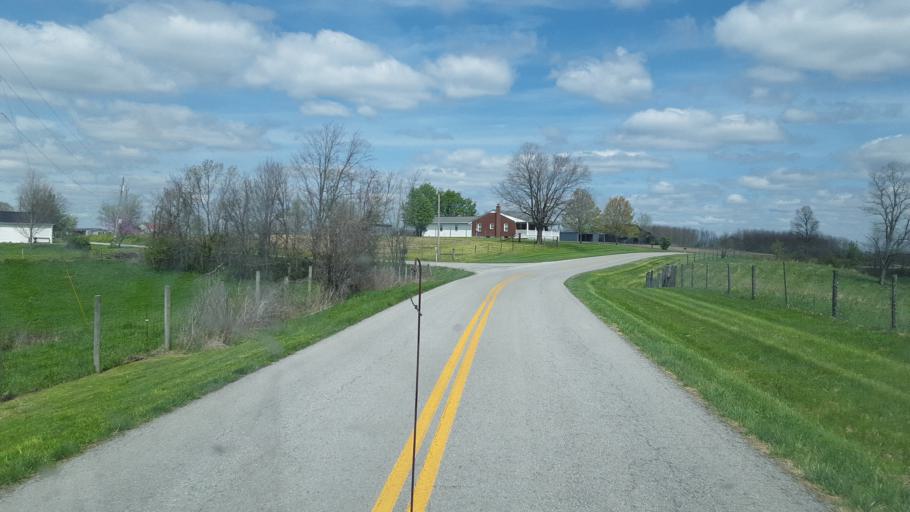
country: US
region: Kentucky
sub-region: Owen County
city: Owenton
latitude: 38.6223
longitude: -84.7863
